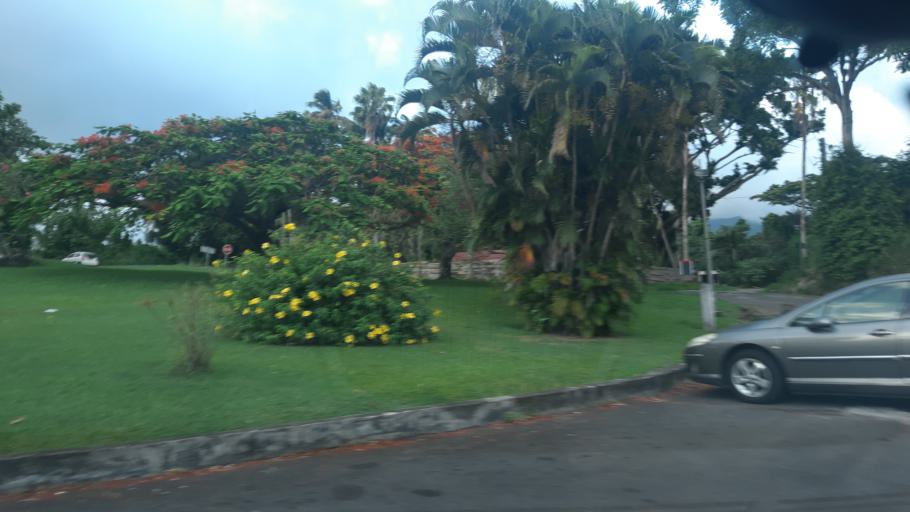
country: GP
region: Guadeloupe
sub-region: Guadeloupe
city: Saint-Claude
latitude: 16.0092
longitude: -61.7098
